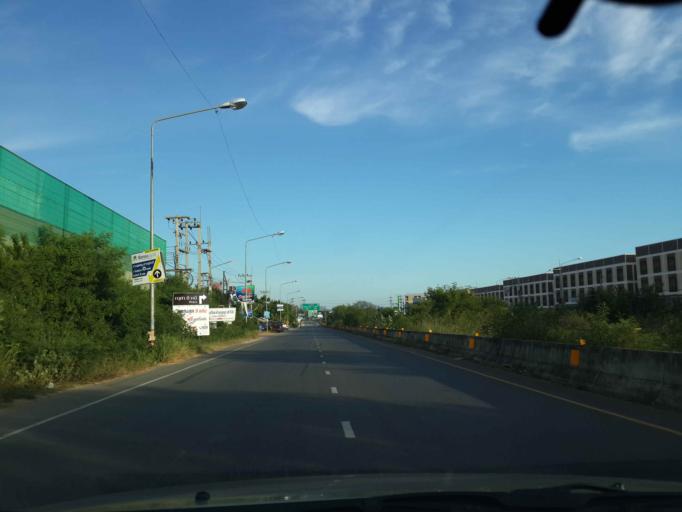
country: TH
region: Chon Buri
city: Phatthaya
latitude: 12.8614
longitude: 100.9134
